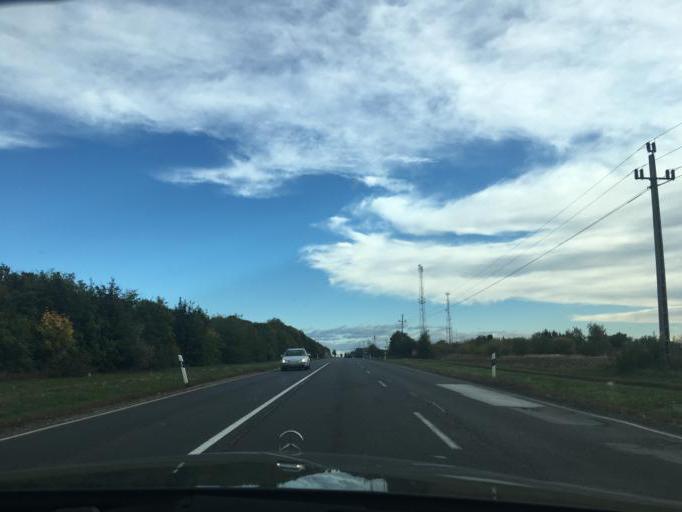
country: HU
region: Borsod-Abauj-Zemplen
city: Onga
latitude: 48.1497
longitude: 20.8939
